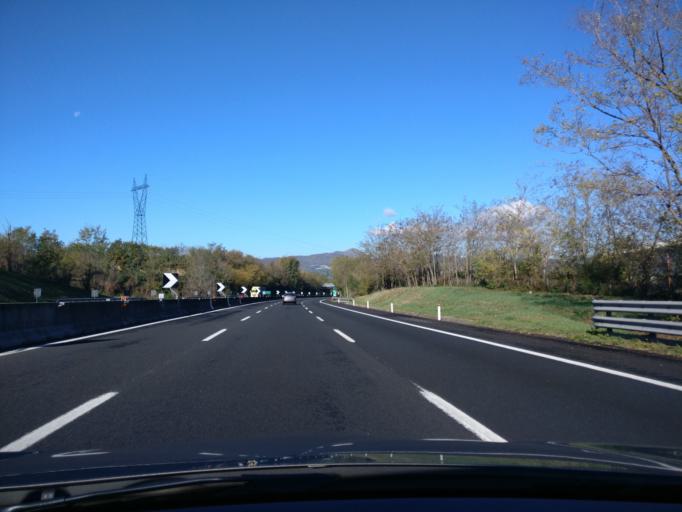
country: IT
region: Campania
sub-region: Provincia di Caserta
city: Zuni
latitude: 41.2154
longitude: 14.1041
